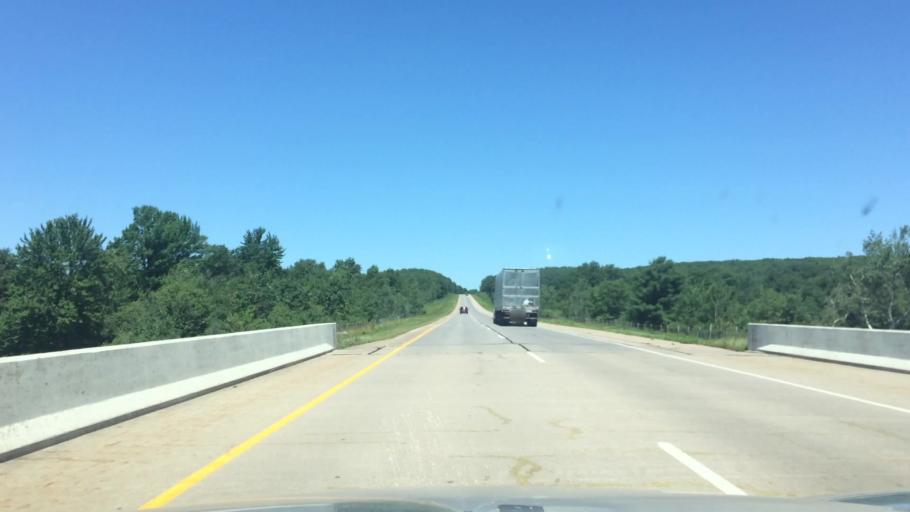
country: US
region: Wisconsin
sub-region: Marathon County
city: Mosinee
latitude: 44.6949
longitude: -89.6444
